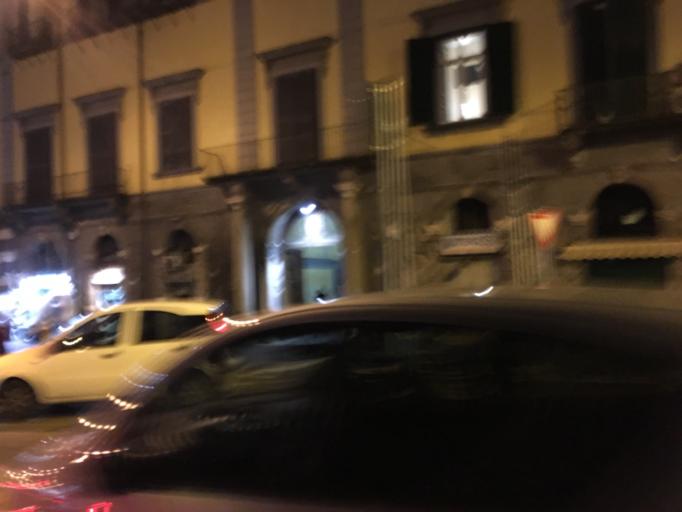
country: IT
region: Campania
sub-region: Provincia di Napoli
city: Napoli
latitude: 40.8324
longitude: 14.2259
